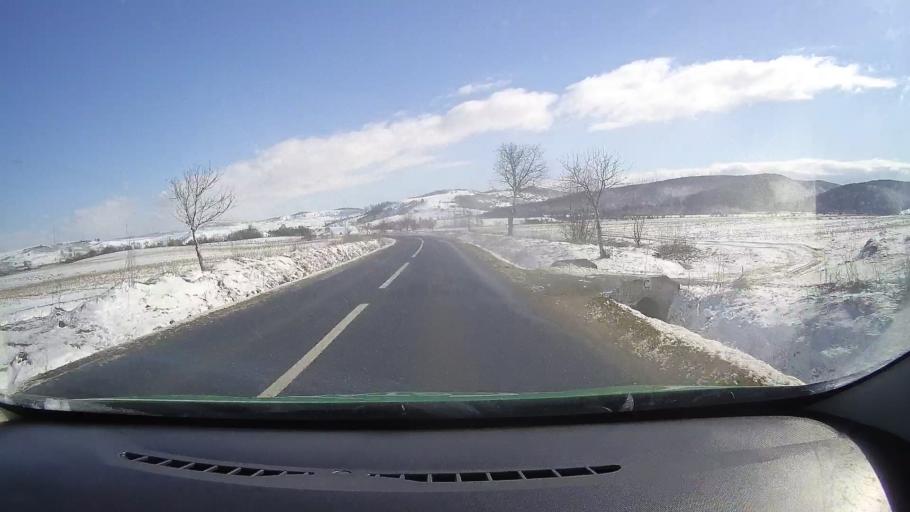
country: RO
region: Sibiu
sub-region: Comuna Rosia
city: Rosia
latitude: 45.7911
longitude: 24.3041
